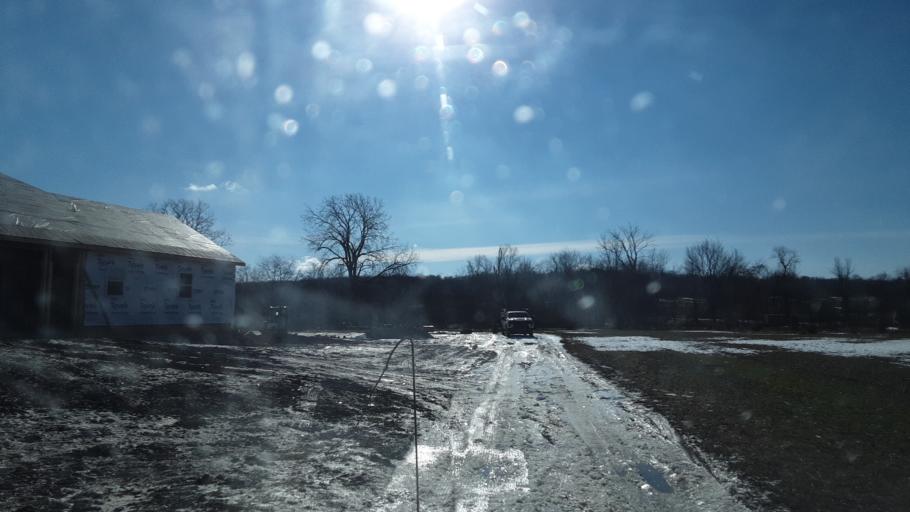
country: US
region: Ohio
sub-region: Richland County
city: Lincoln Heights
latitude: 40.8419
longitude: -82.4858
